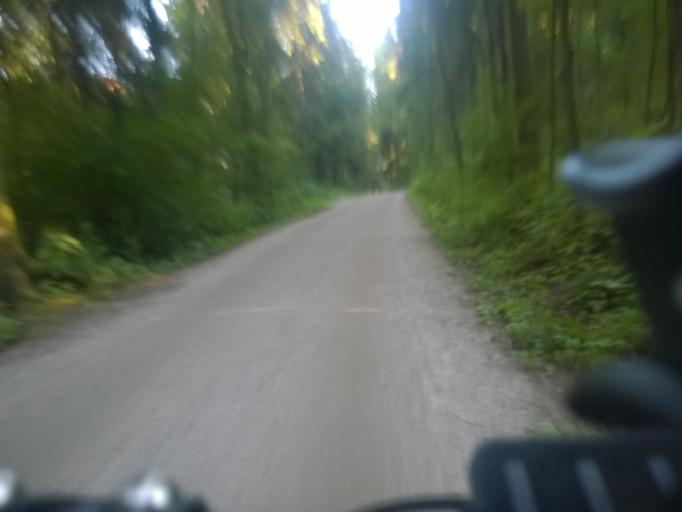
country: FI
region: Uusimaa
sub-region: Helsinki
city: Helsinki
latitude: 60.1983
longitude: 24.9206
